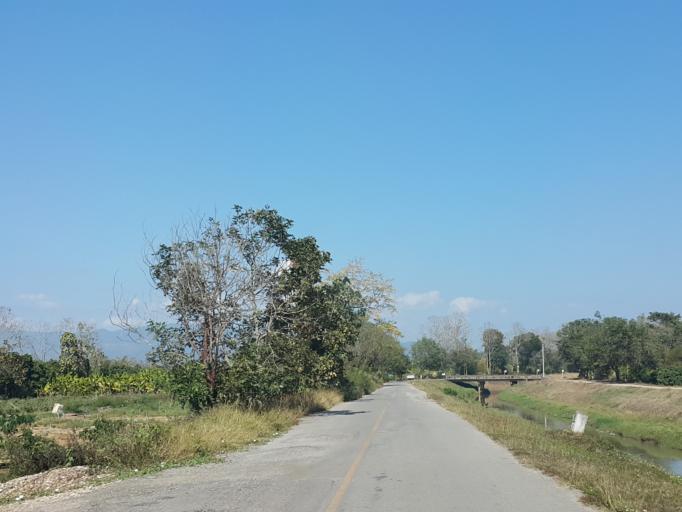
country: TH
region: Chiang Mai
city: Mae Taeng
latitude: 19.0891
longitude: 98.9501
